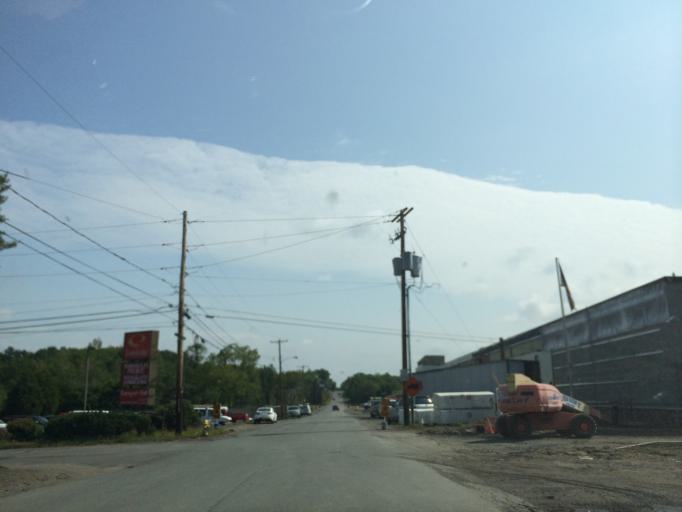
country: US
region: Pennsylvania
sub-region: Lackawanna County
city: Taylor
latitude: 41.3735
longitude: -75.6785
